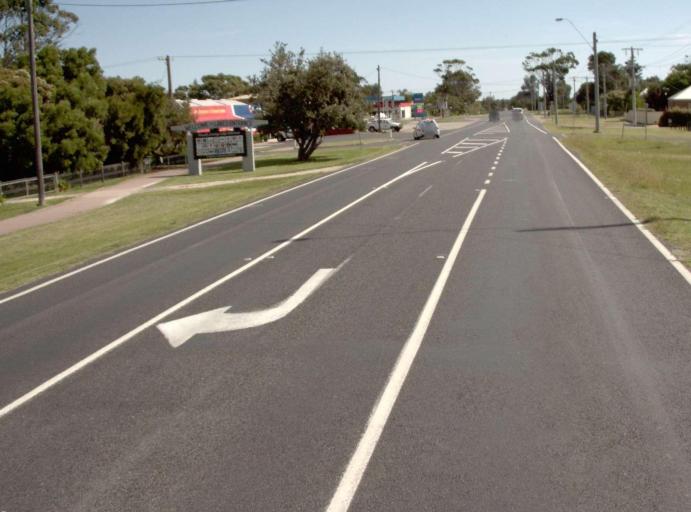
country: AU
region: Victoria
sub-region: East Gippsland
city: Lakes Entrance
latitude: -37.8732
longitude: 148.0091
